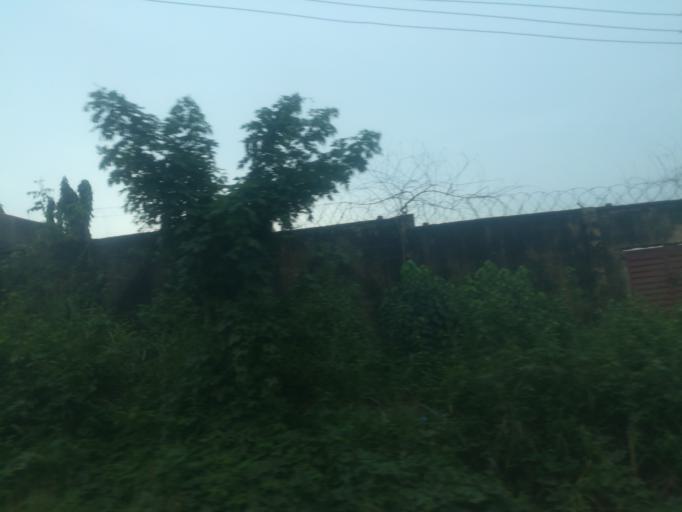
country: NG
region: Oyo
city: Ibadan
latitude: 7.3530
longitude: 3.8223
